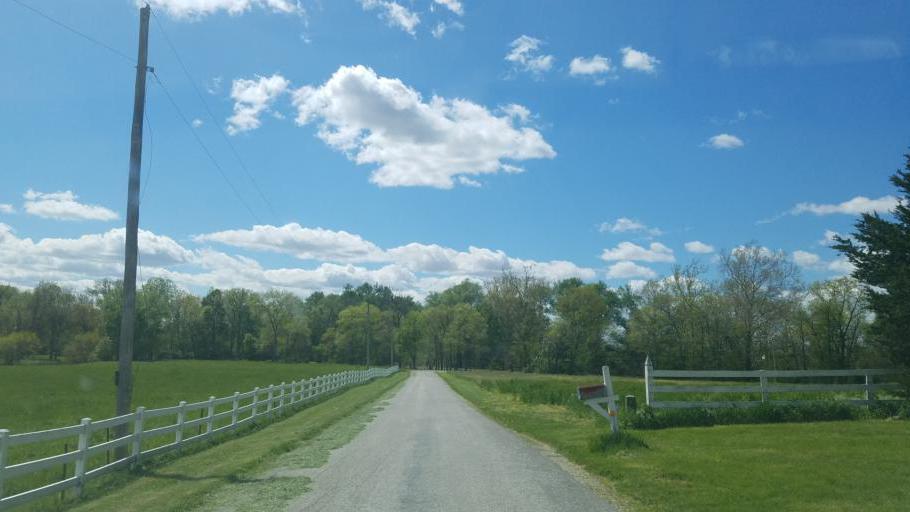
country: US
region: Ohio
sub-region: Marion County
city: Prospect
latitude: 40.3853
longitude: -83.1861
